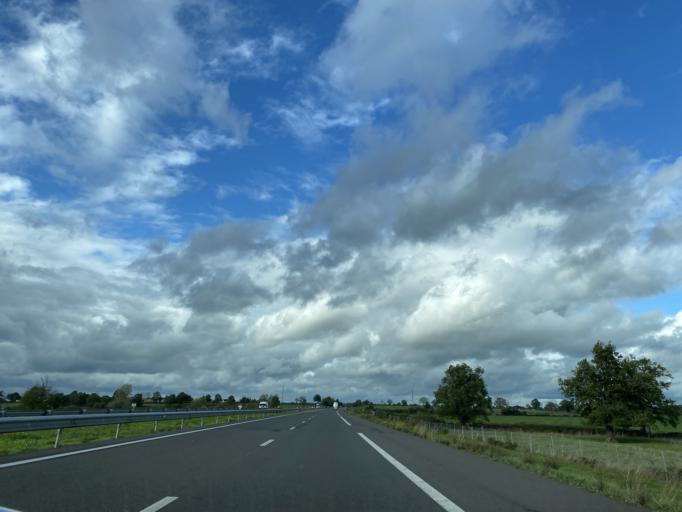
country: FR
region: Auvergne
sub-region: Departement de l'Allier
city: Bellenaves
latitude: 46.2699
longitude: 3.0594
